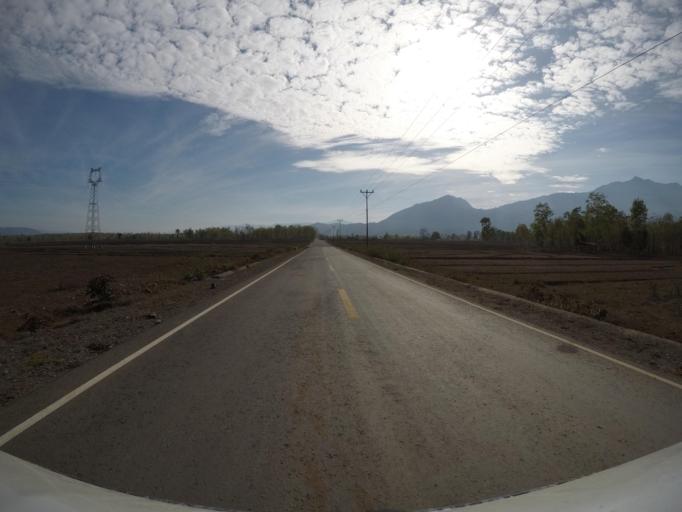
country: TL
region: Bobonaro
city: Maliana
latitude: -8.9328
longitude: 125.1978
